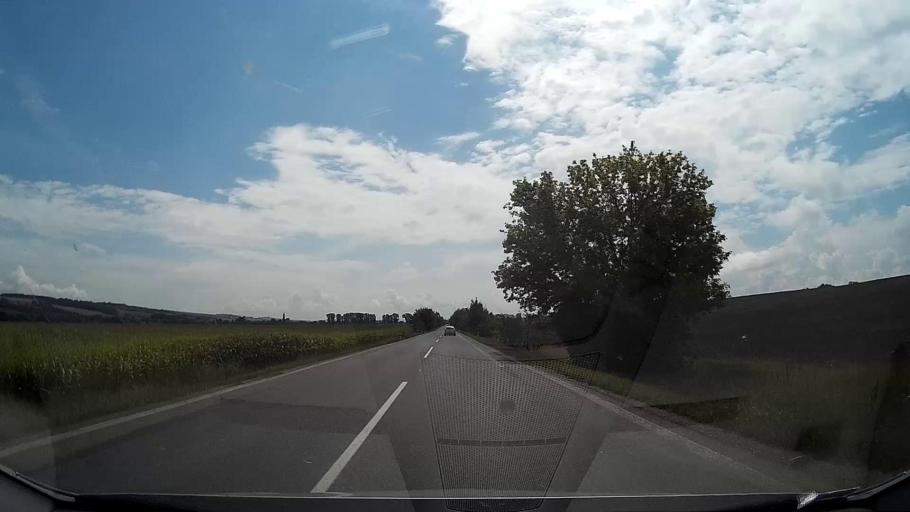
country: SK
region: Banskobystricky
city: Rimavska Sobota
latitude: 48.4182
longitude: 19.9694
